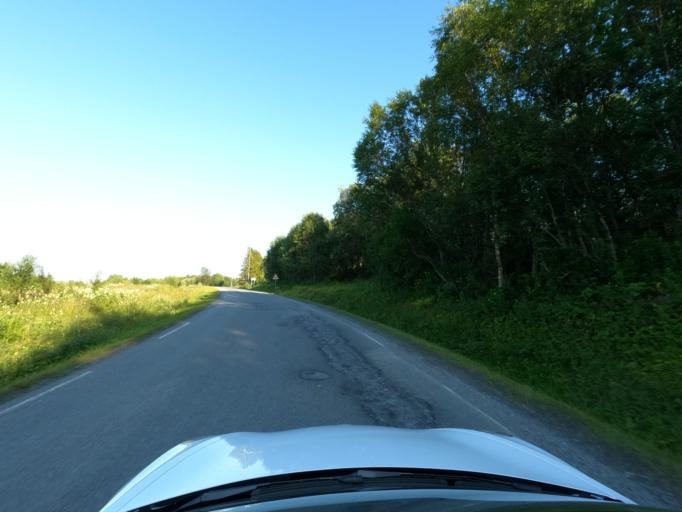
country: NO
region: Nordland
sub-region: Evenes
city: Randa
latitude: 68.4903
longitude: 16.8957
